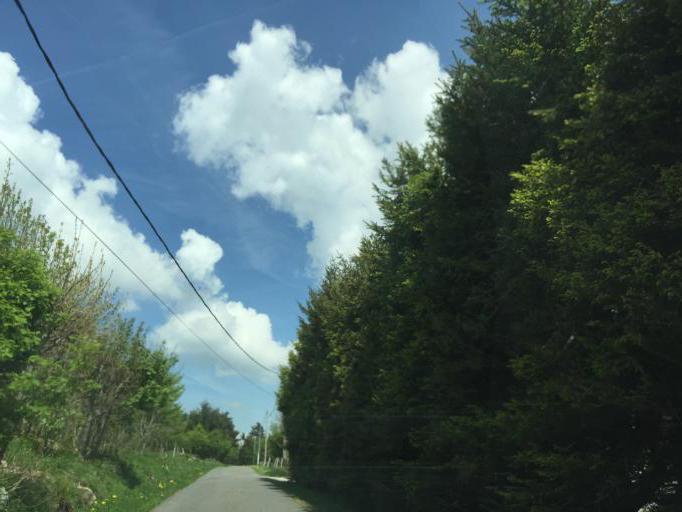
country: FR
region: Rhone-Alpes
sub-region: Departement de la Loire
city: Saint-Sauveur-en-Rue
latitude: 45.2865
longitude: 4.4780
